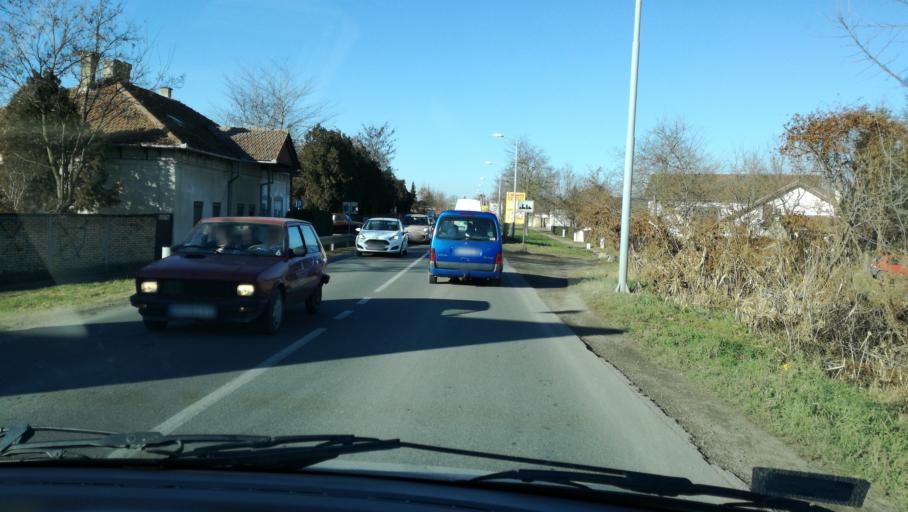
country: RS
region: Autonomna Pokrajina Vojvodina
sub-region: Severnobacki Okrug
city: Subotica
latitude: 46.0853
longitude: 19.6884
